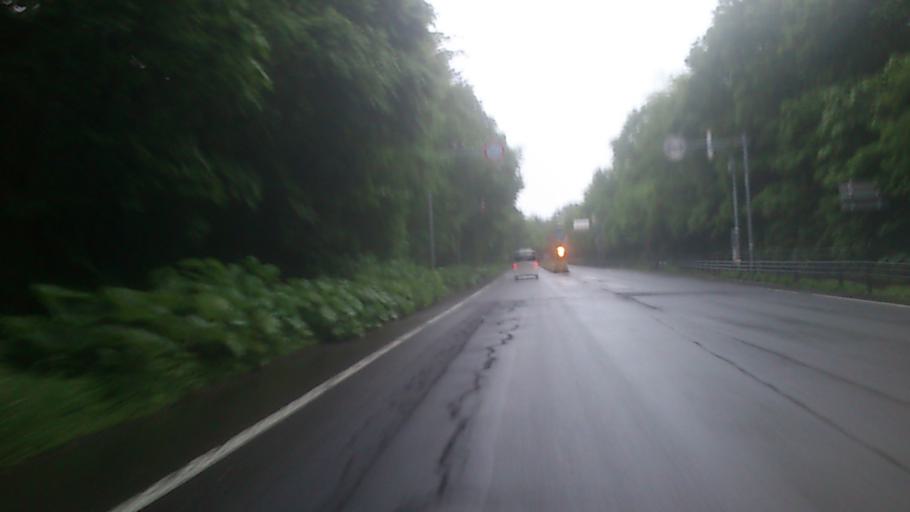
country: JP
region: Hokkaido
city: Chitose
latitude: 42.8013
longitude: 141.5680
